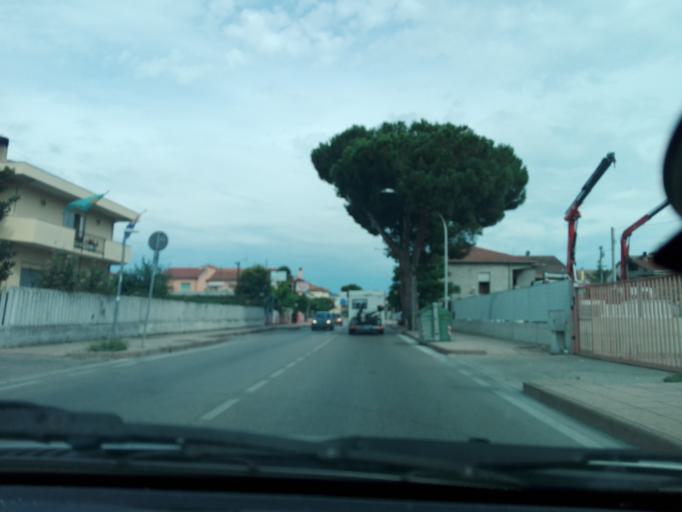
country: IT
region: Abruzzo
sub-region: Provincia di Pescara
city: San Martino Bassa
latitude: 42.5251
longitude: 14.1396
